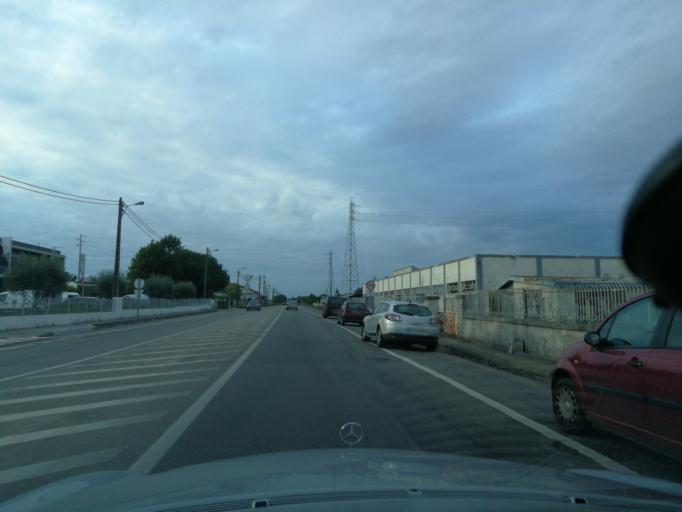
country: PT
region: Aveiro
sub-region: Agueda
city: Agueda
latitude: 40.5953
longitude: -8.4575
